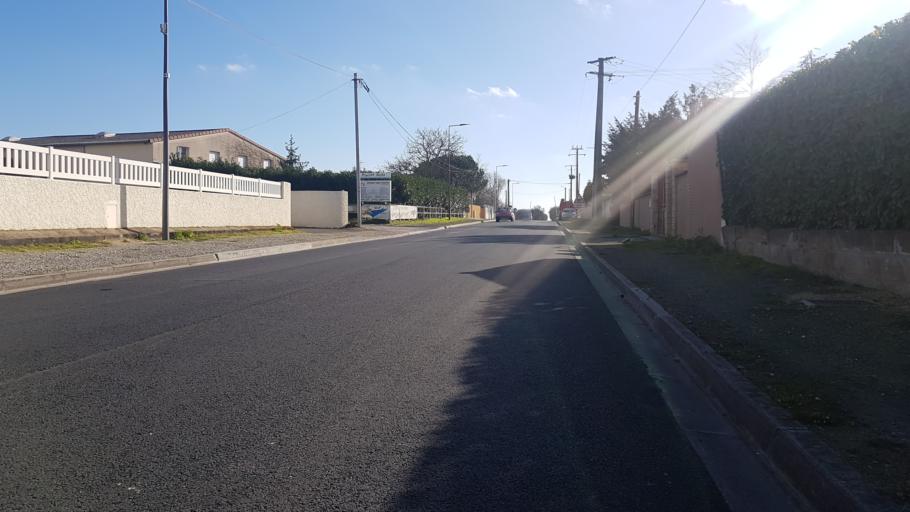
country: FR
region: Poitou-Charentes
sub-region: Departement de la Vienne
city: Avanton
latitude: 46.6589
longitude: 0.3049
